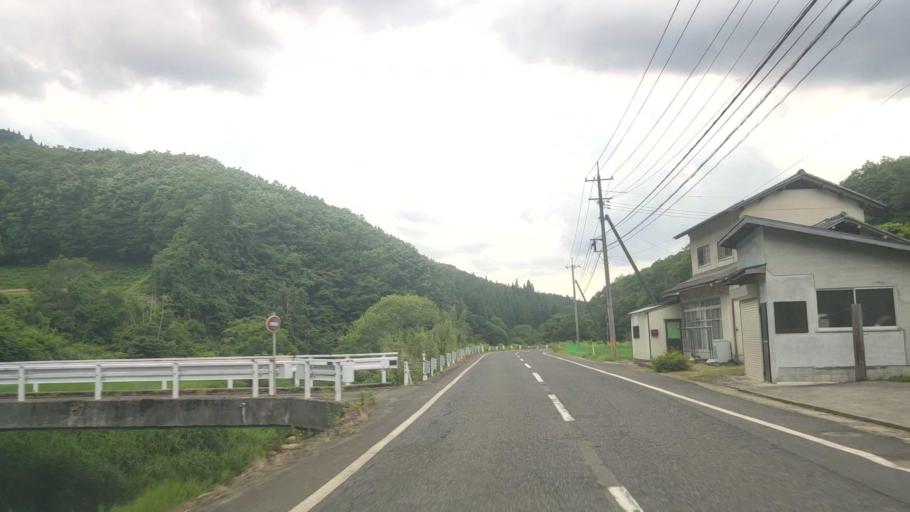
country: JP
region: Tottori
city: Kurayoshi
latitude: 35.2940
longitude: 133.9799
